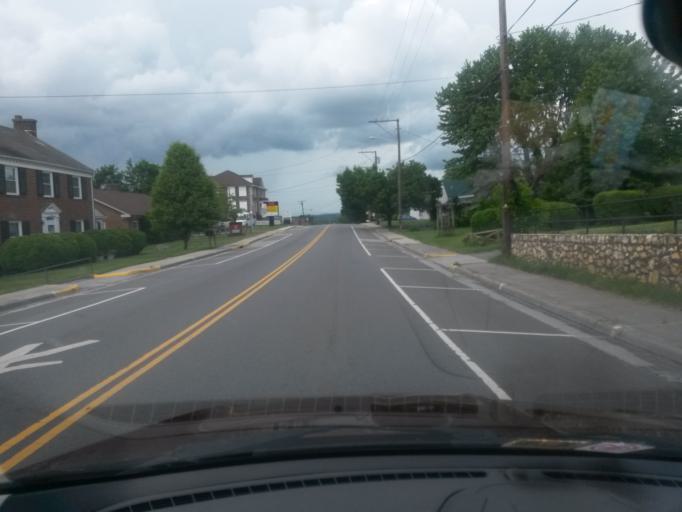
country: US
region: Virginia
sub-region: Floyd County
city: Floyd
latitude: 36.9126
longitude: -80.3205
